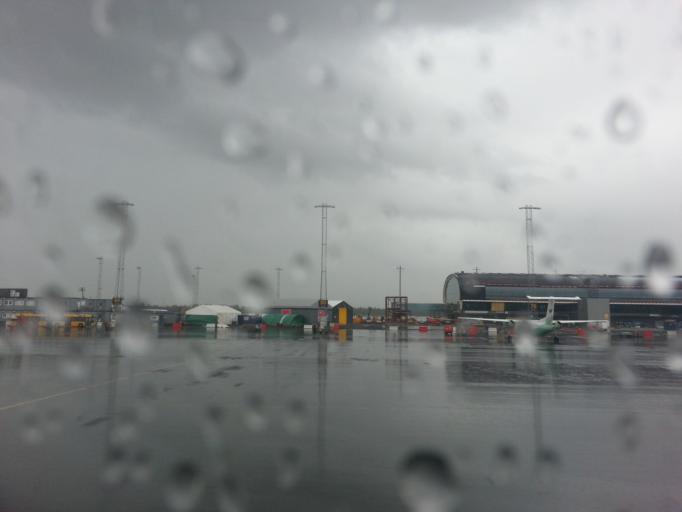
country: NO
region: Akershus
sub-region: Nannestad
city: Teigebyen
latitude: 60.1983
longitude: 11.0962
